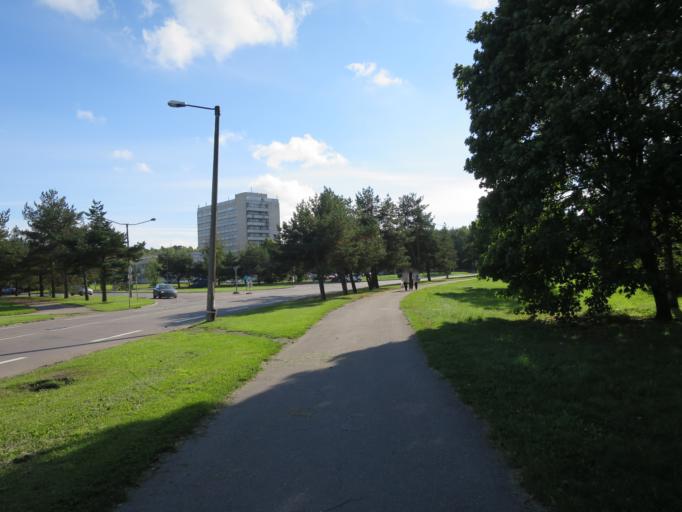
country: EE
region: Harju
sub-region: Tallinna linn
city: Tallinn
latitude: 59.3981
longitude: 24.6976
